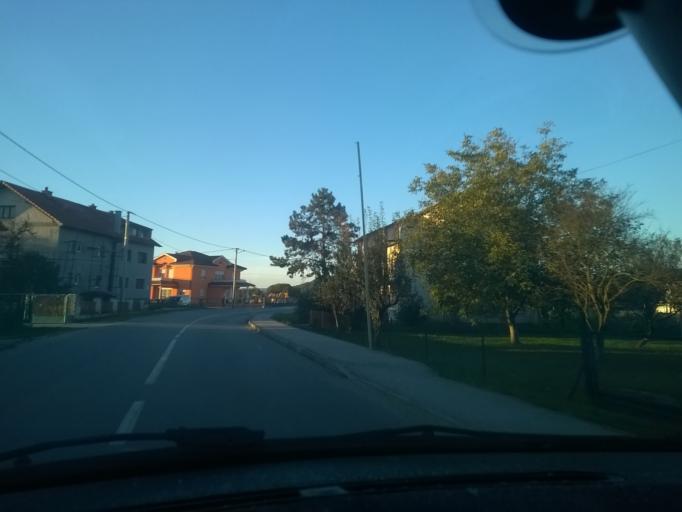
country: HR
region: Krapinsko-Zagorska
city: Zabok
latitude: 46.0872
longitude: 15.9053
